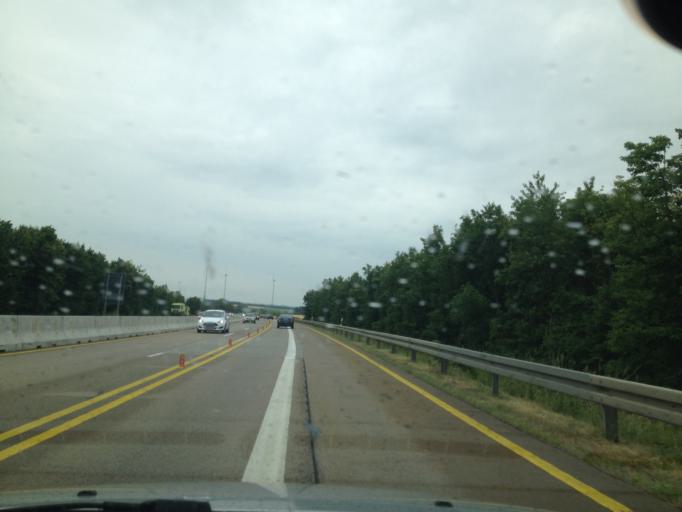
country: DE
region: Bavaria
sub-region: Regierungsbezirk Mittelfranken
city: Gollhofen
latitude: 49.5305
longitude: 10.1883
